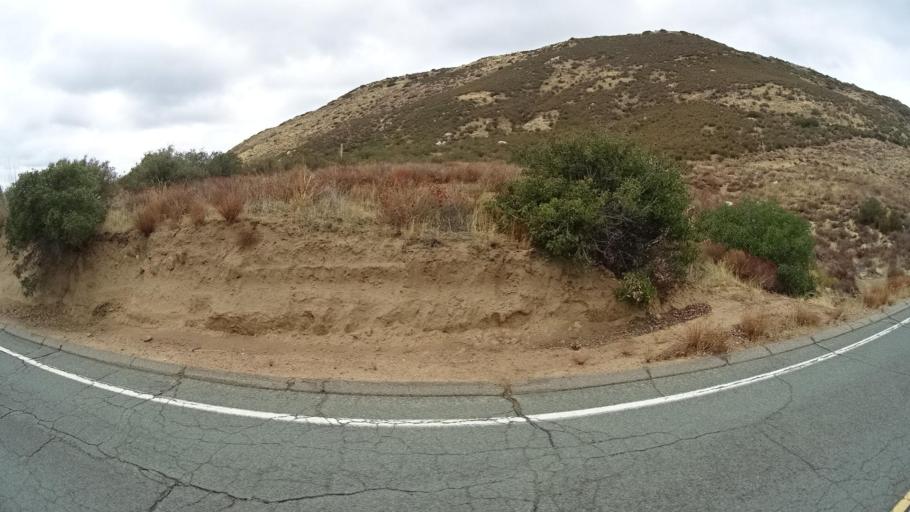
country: US
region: California
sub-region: San Diego County
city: Pine Valley
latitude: 32.7366
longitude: -116.4533
